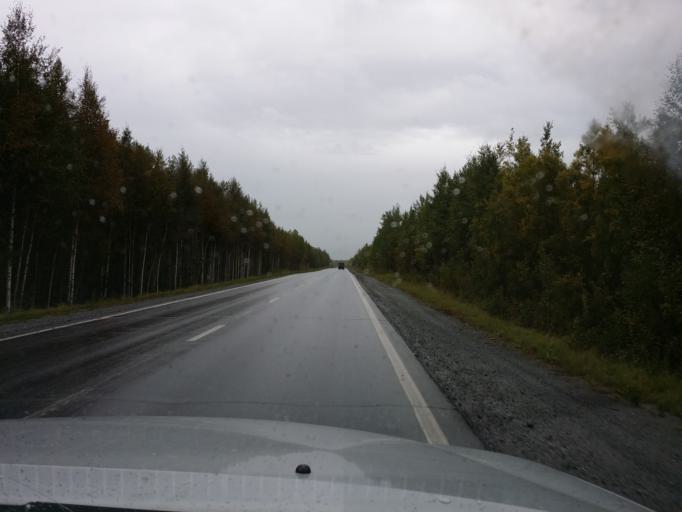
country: RU
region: Khanty-Mansiyskiy Avtonomnyy Okrug
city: Langepas
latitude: 61.1661
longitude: 75.5817
